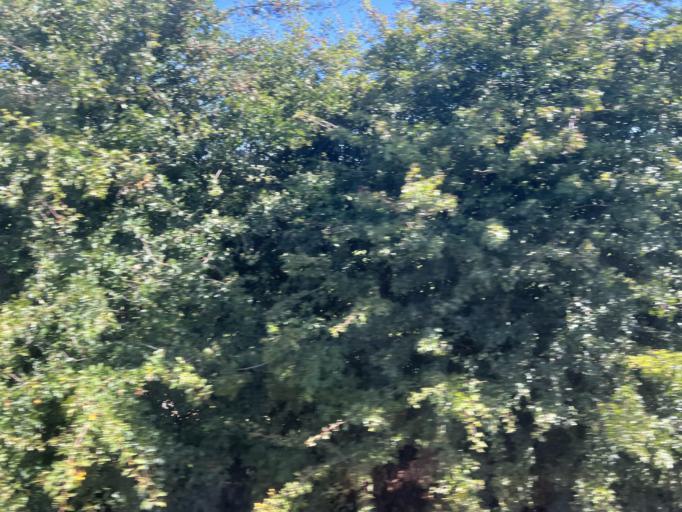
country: GB
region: England
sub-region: Lincolnshire
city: Wainfleet All Saints
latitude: 53.1339
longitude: 0.1907
